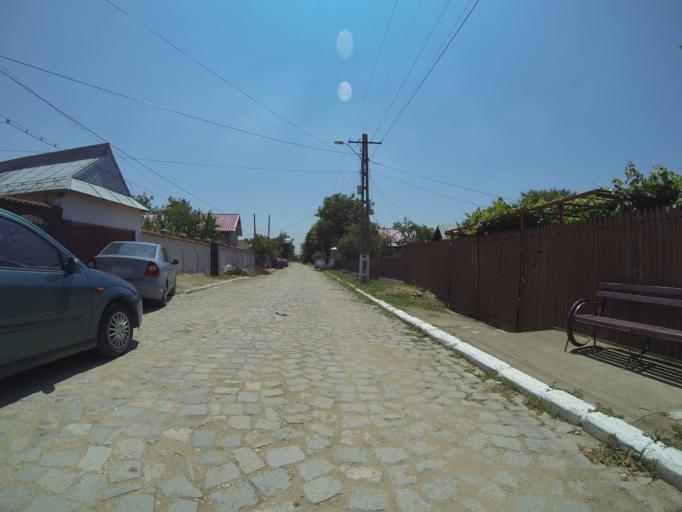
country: RO
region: Dolj
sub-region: Comuna Segarcea
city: Segarcea
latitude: 44.0925
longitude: 23.7504
